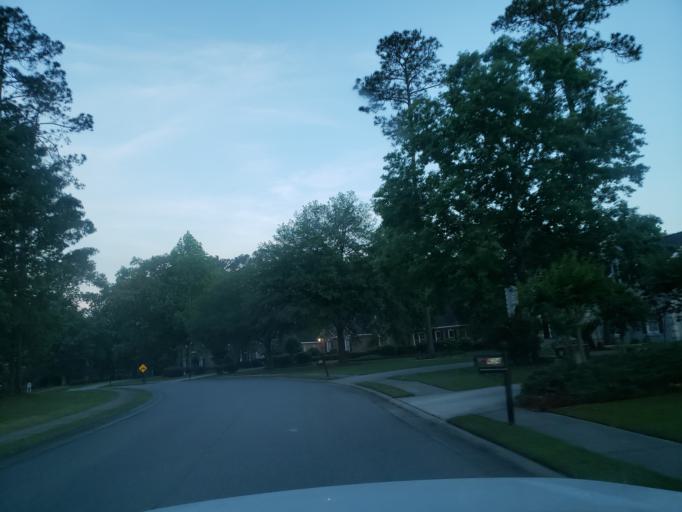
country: US
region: Georgia
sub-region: Chatham County
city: Pooler
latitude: 32.0716
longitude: -81.2333
